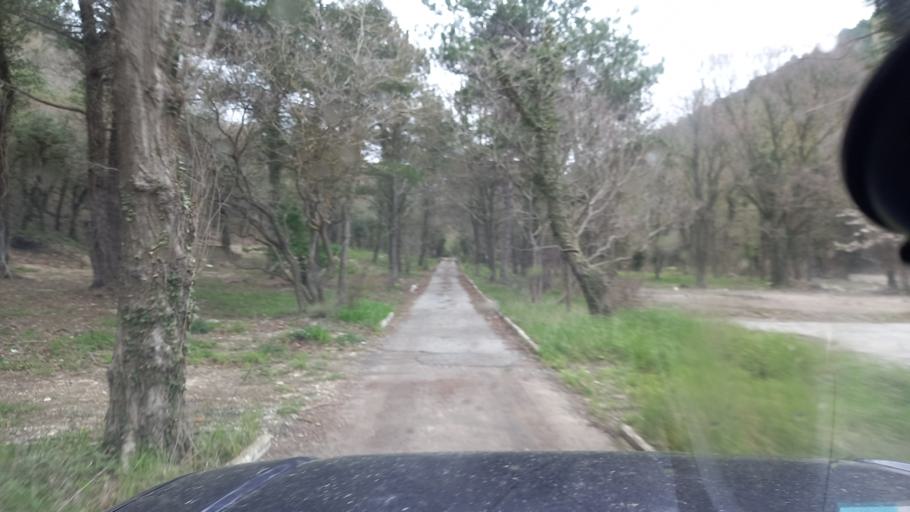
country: RU
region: Krasnodarskiy
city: Arkhipo-Osipovka
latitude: 44.3696
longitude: 38.4495
